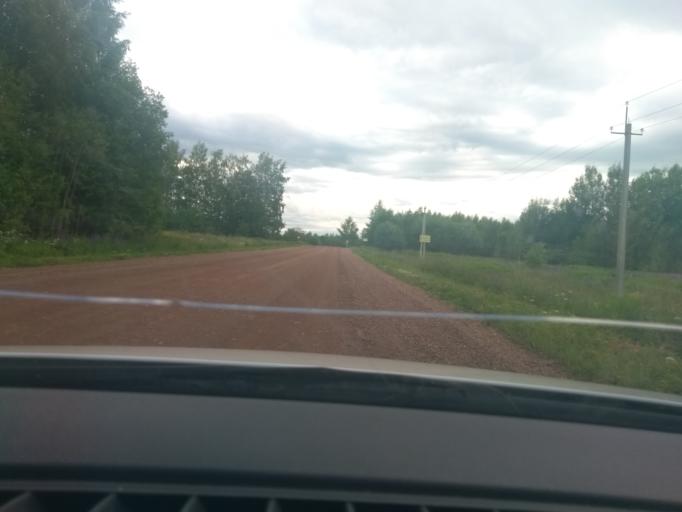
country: RU
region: Perm
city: Sylva
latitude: 57.8169
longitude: 56.7267
